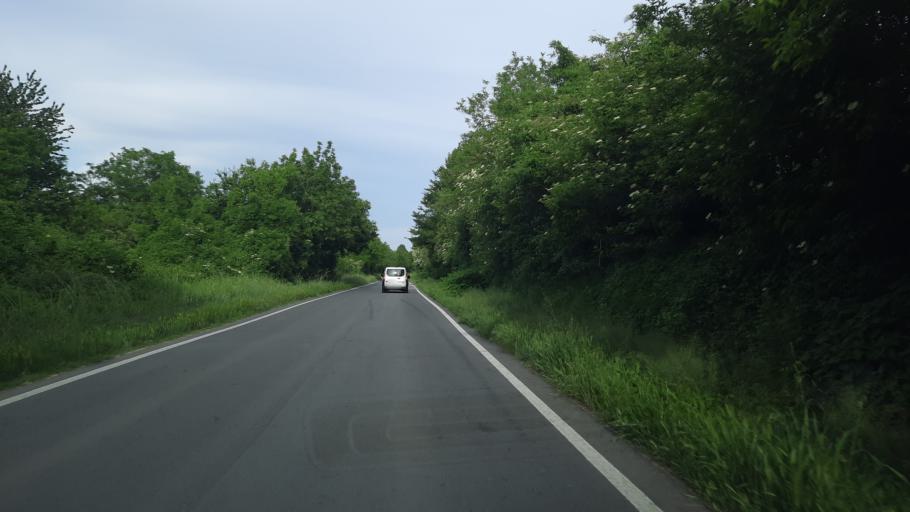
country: IT
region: Piedmont
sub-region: Provincia di Alessandria
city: San Giorgio Monferrato
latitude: 45.1354
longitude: 8.4221
